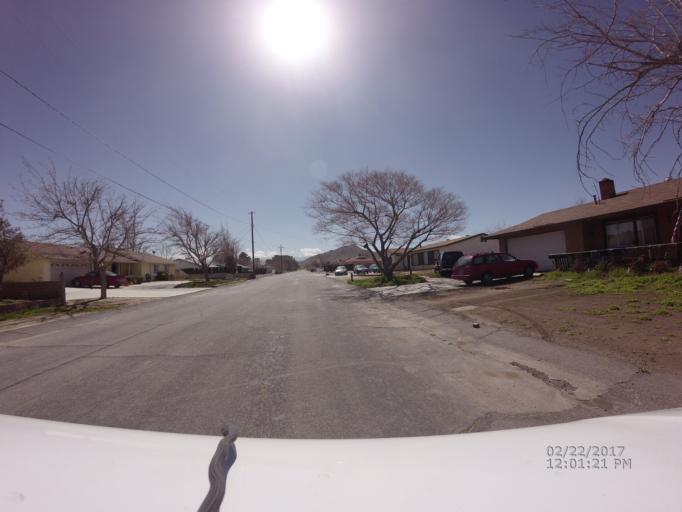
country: US
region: California
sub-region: Los Angeles County
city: Lake Los Angeles
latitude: 34.6207
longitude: -117.8347
